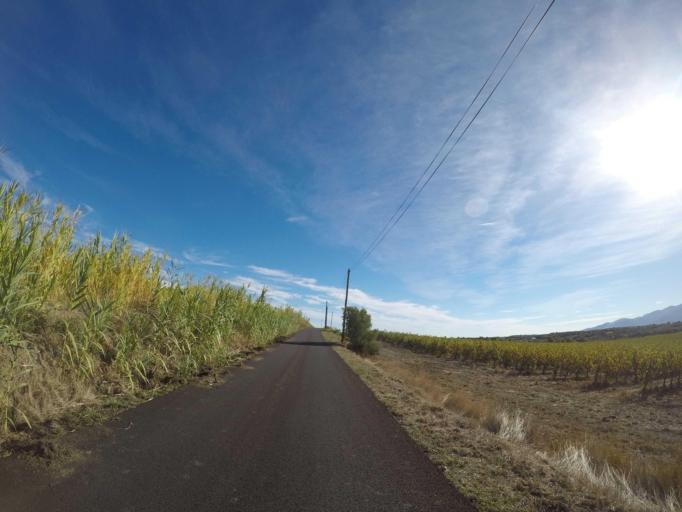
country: FR
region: Languedoc-Roussillon
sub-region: Departement des Pyrenees-Orientales
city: Trouillas
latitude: 42.5728
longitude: 2.8000
